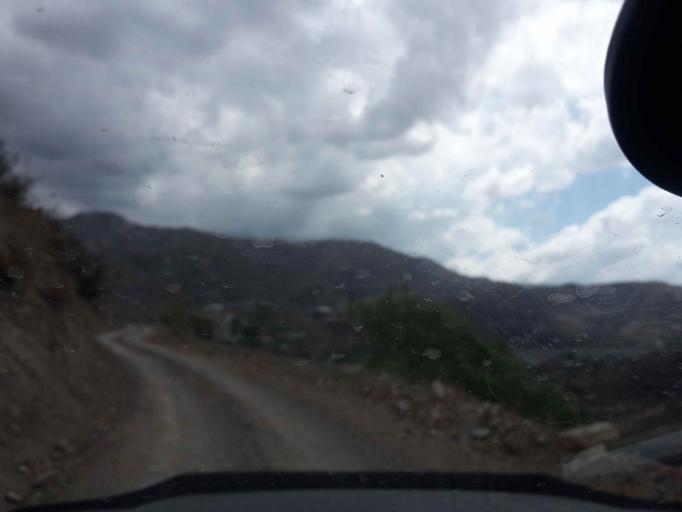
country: BO
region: Cochabamba
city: Colchani
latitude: -17.5160
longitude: -66.6108
